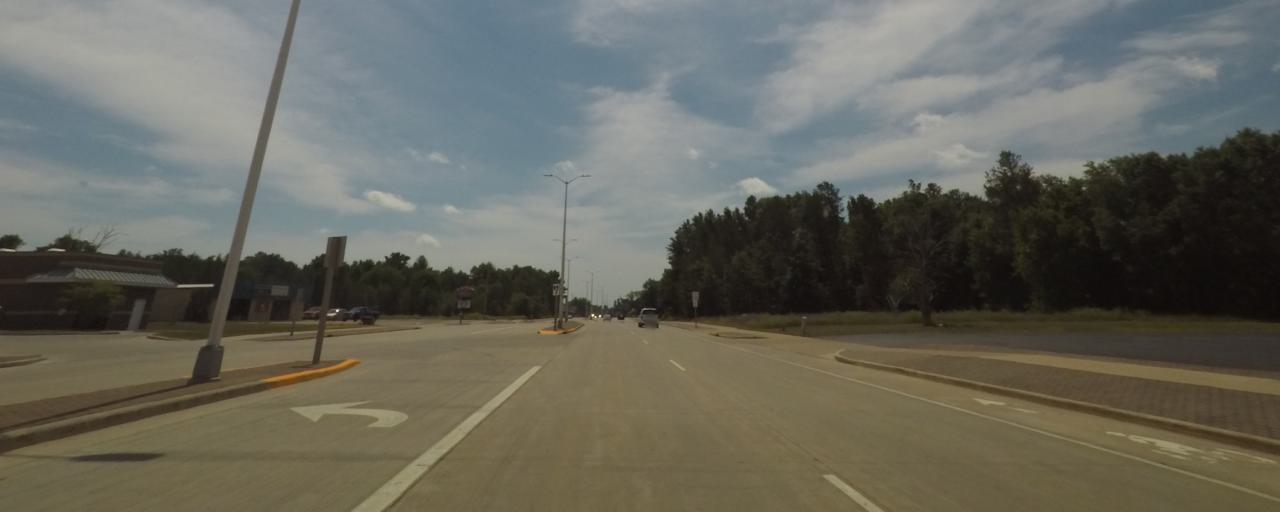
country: US
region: Wisconsin
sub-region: Portage County
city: Plover
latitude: 44.4687
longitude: -89.5465
